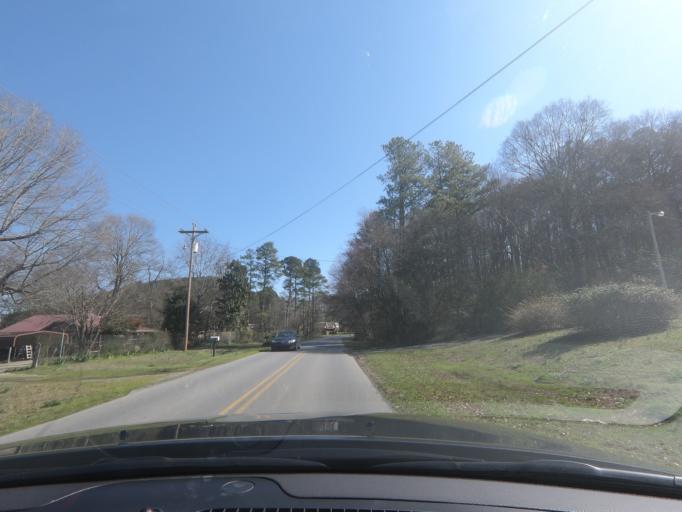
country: US
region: Georgia
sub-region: Gordon County
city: Calhoun
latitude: 34.4624
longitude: -85.0020
